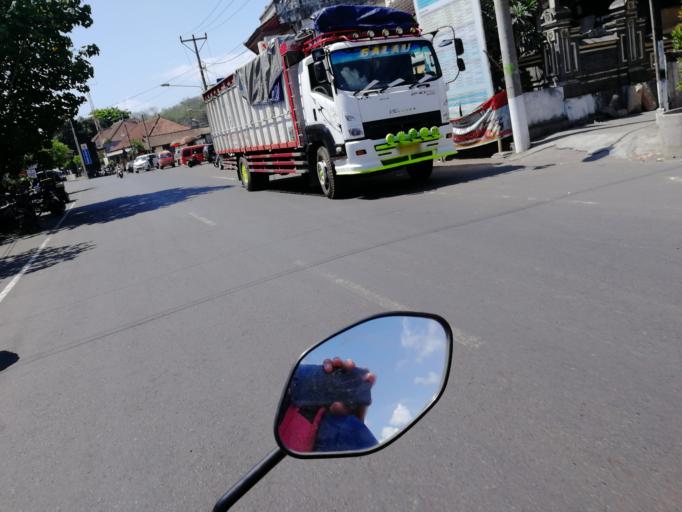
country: ID
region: Bali
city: Padangbai
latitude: -8.5319
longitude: 115.5067
